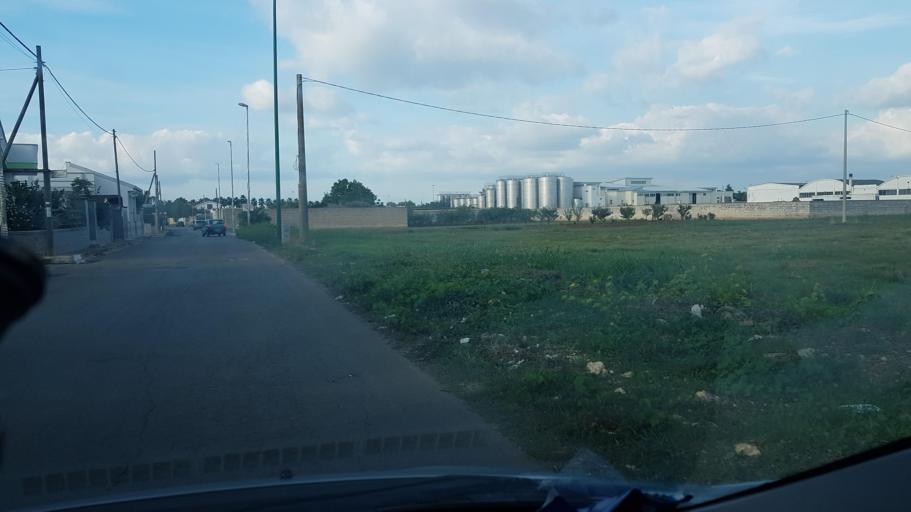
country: IT
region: Apulia
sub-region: Provincia di Lecce
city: Veglie
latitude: 40.3437
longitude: 17.9663
